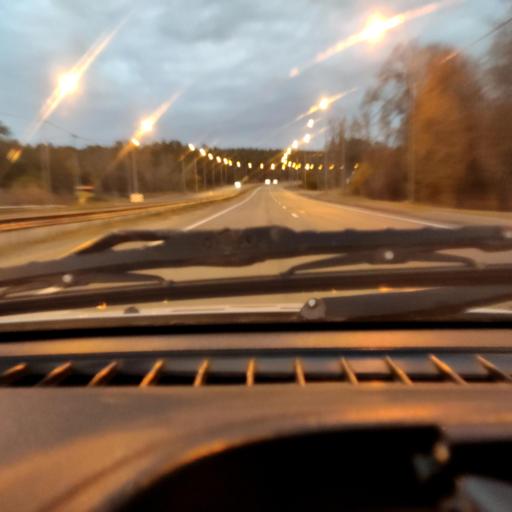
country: RU
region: Samara
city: Zhigulevsk
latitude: 53.5303
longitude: 49.5199
